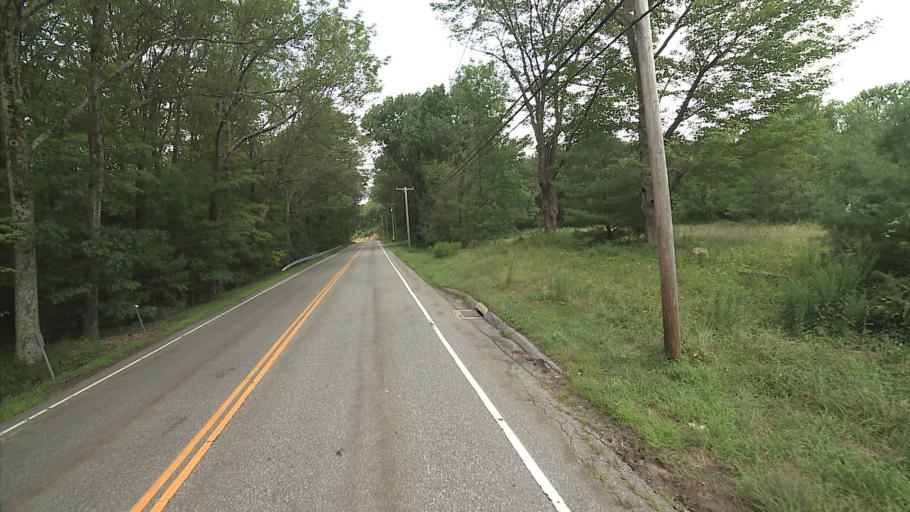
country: US
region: Massachusetts
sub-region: Hampden County
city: Holland
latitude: 41.9999
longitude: -72.1509
